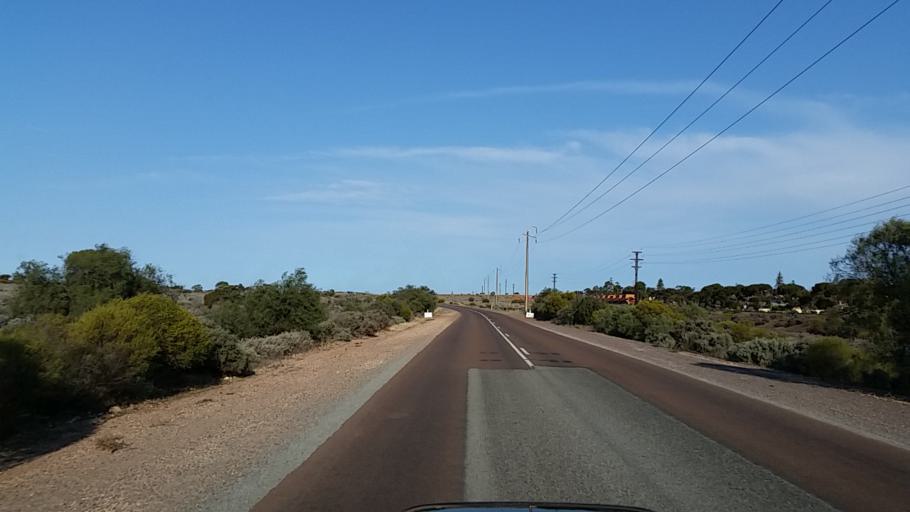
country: AU
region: South Australia
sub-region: Whyalla
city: Whyalla
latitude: -33.0141
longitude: 137.5485
